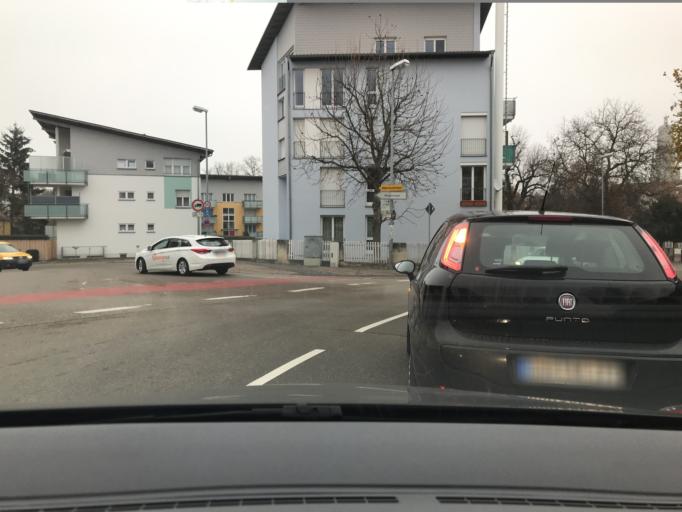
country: DE
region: Bavaria
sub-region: Swabia
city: Noerdlingen
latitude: 48.8483
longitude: 10.4826
